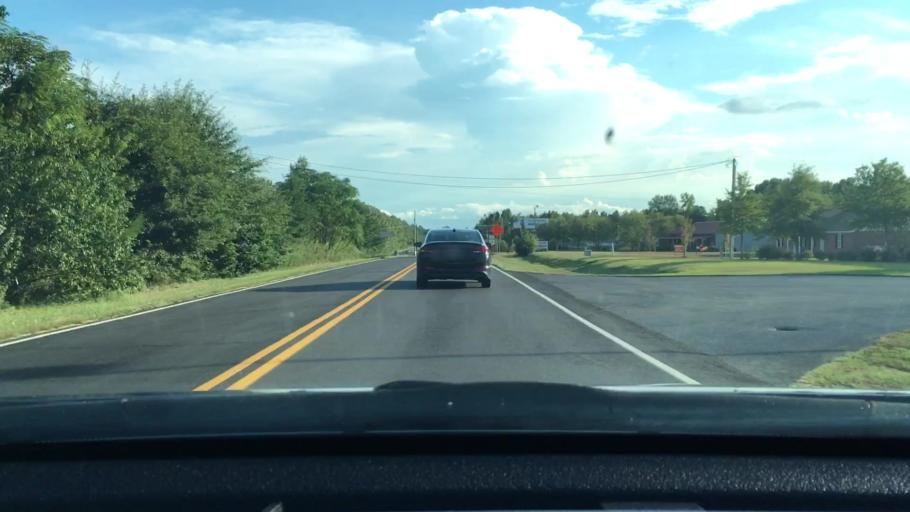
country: US
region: South Carolina
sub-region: Sumter County
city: South Sumter
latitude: 33.8837
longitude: -80.3507
